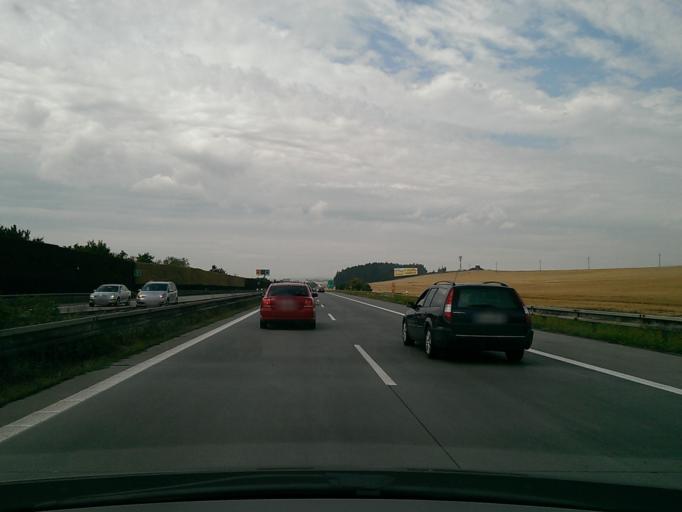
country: CZ
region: Vysocina
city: Merin
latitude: 49.3931
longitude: 15.8966
